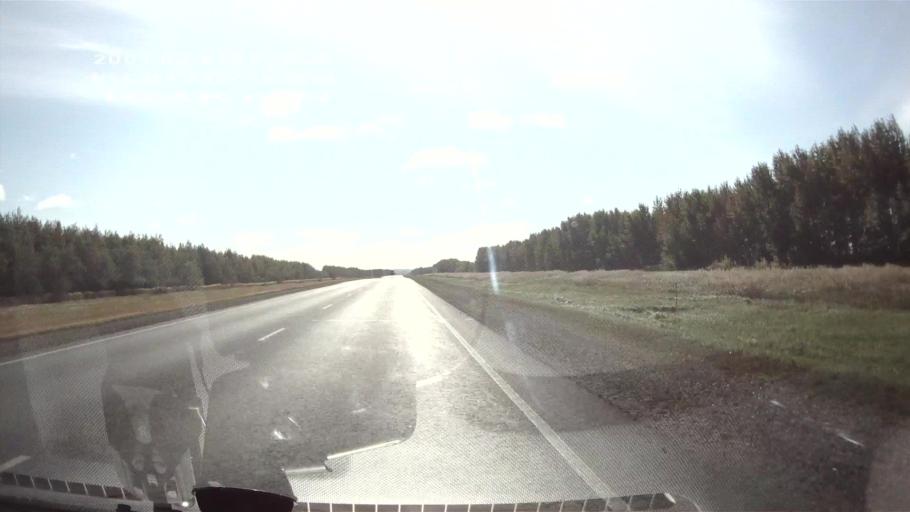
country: RU
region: Ulyanovsk
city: Tsil'na
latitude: 54.5635
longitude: 47.9211
